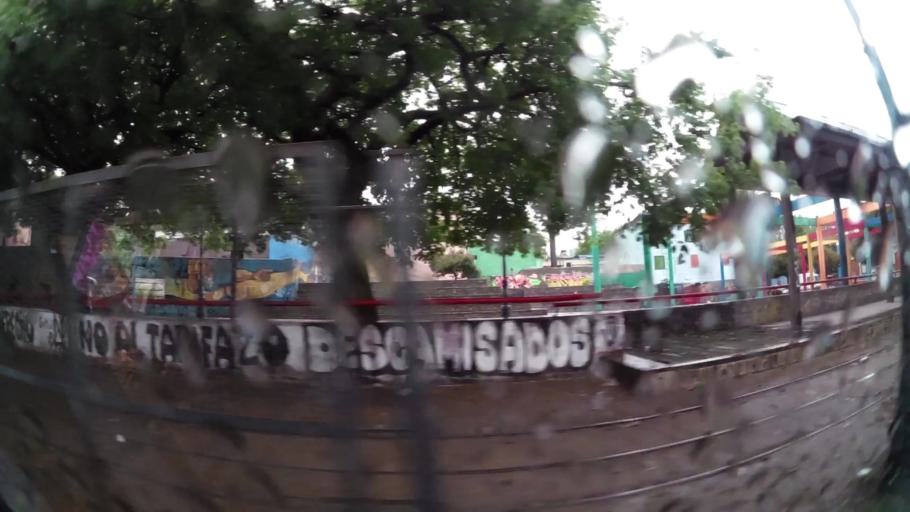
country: AR
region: Buenos Aires
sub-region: Partido de Avellaneda
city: Avellaneda
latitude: -34.6390
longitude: -58.3638
